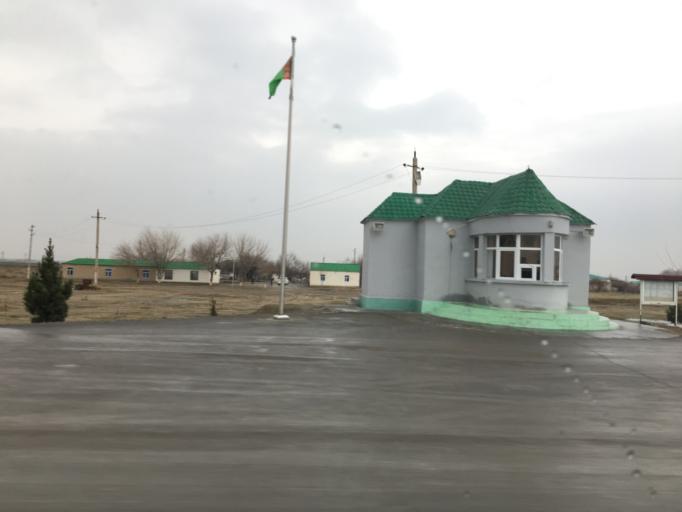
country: TM
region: Ahal
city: Annau
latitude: 37.8304
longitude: 58.7448
